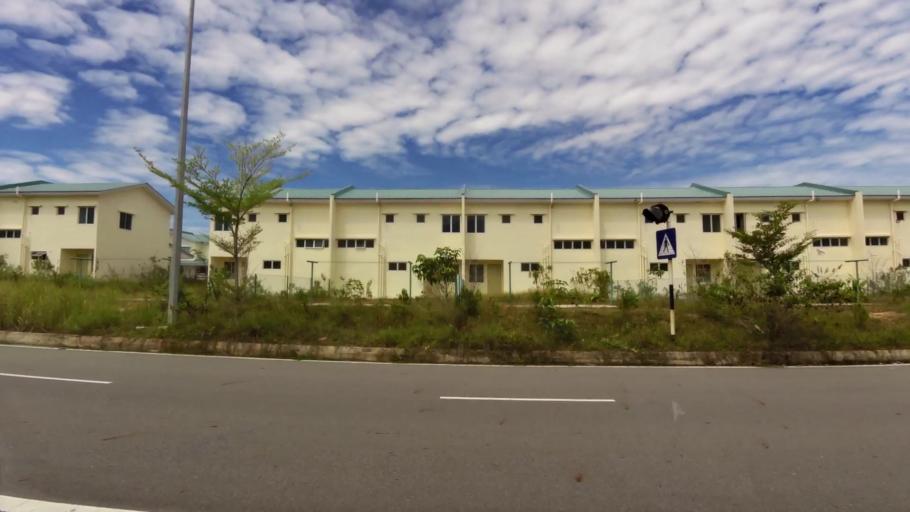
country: BN
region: Brunei and Muara
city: Bandar Seri Begawan
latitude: 4.9731
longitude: 115.0109
